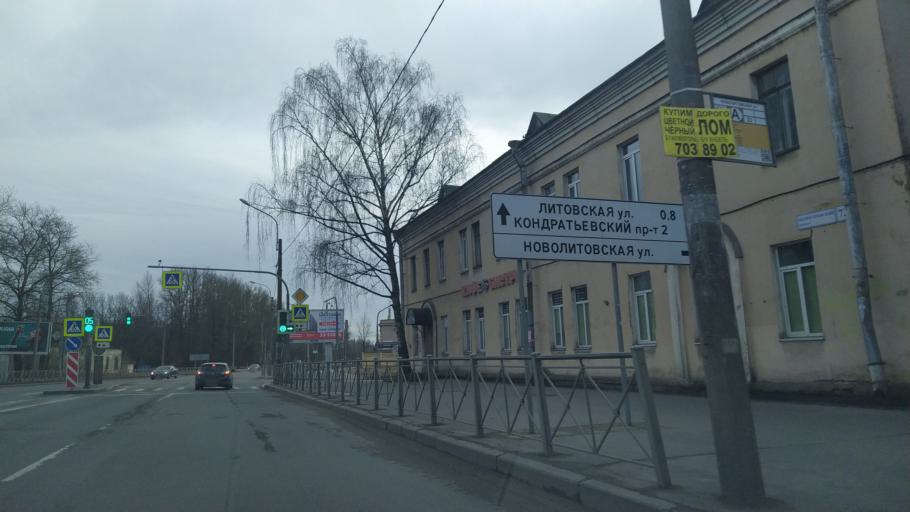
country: RU
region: St.-Petersburg
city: Kushelevka
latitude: 59.9842
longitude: 30.3617
